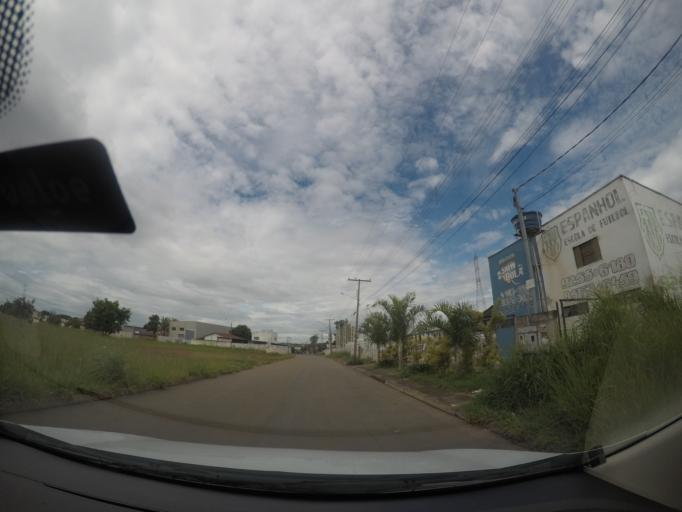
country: BR
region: Goias
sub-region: Goiania
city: Goiania
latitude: -16.7387
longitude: -49.3445
